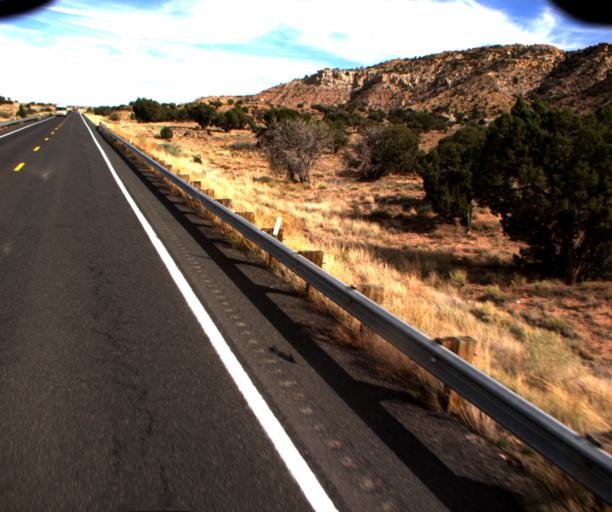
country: US
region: Arizona
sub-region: Navajo County
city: Kayenta
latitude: 36.6948
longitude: -110.3564
